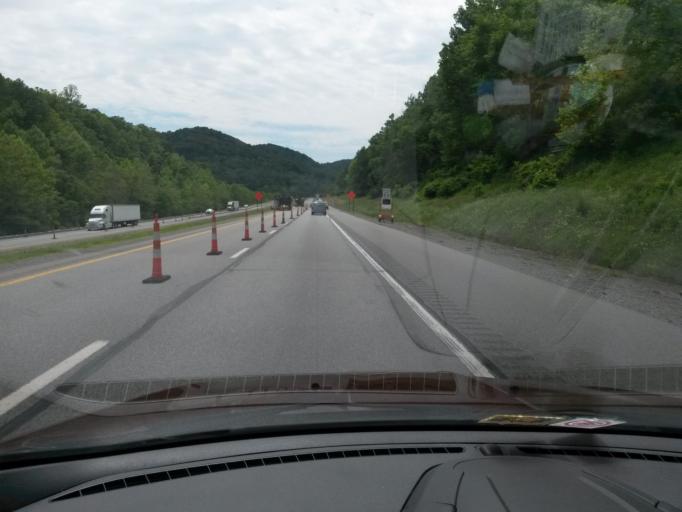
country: US
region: West Virginia
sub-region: Braxton County
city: Sutton
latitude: 38.7602
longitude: -80.6808
